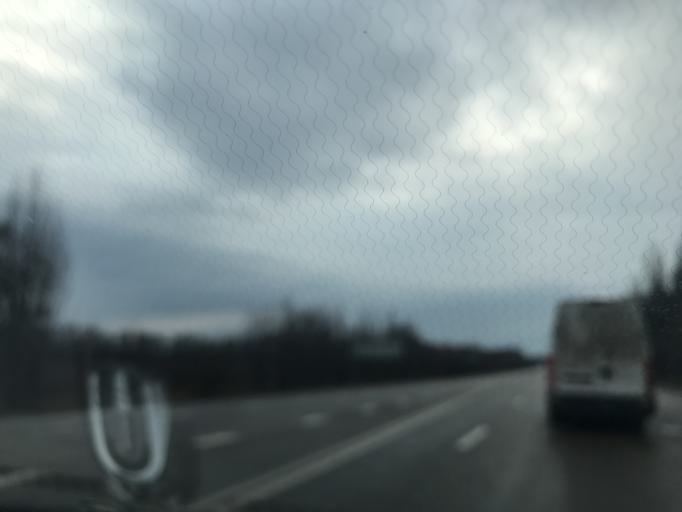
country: RU
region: Krasnodarskiy
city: Tikhoretsk
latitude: 45.8797
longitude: 40.1368
